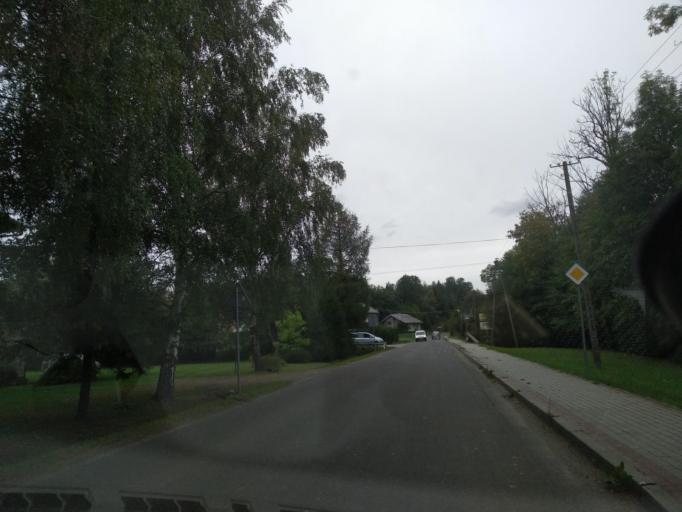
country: PL
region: Subcarpathian Voivodeship
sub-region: Powiat krosnienski
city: Iwonicz-Zdroj
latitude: 49.5831
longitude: 21.7507
